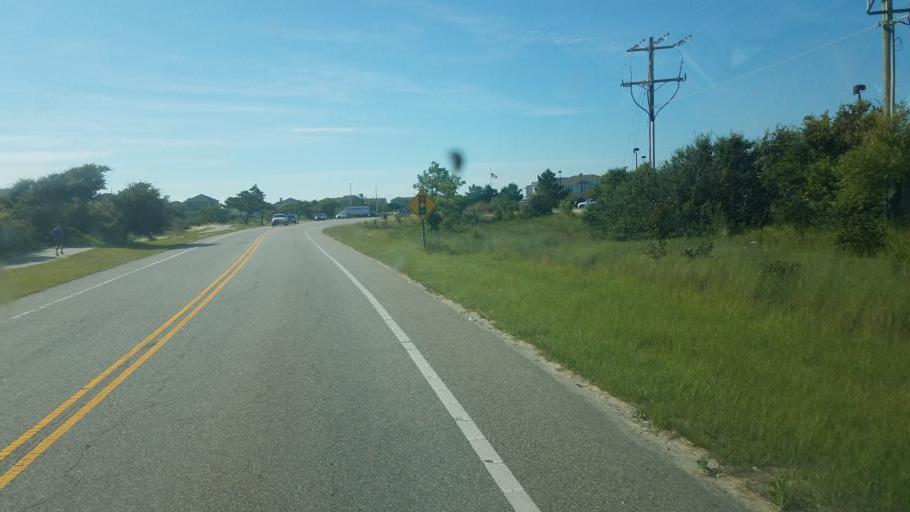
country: US
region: North Carolina
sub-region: Dare County
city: Southern Shores
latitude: 36.3039
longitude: -75.8056
